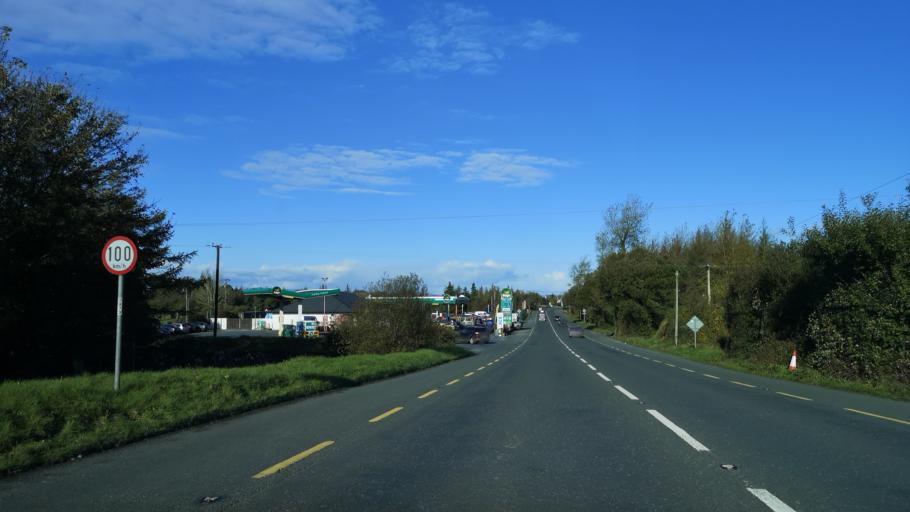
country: IE
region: Connaught
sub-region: County Galway
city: Moycullen
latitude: 53.4491
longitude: -9.0906
